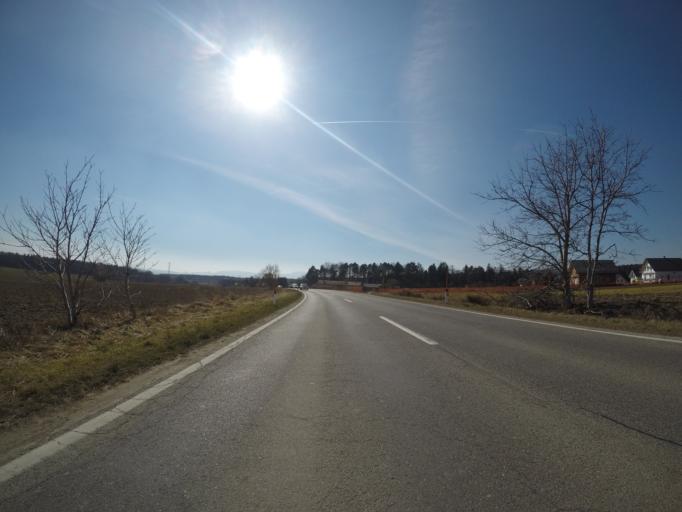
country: SI
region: Race-Fram
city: Fram
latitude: 46.4463
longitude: 15.6370
